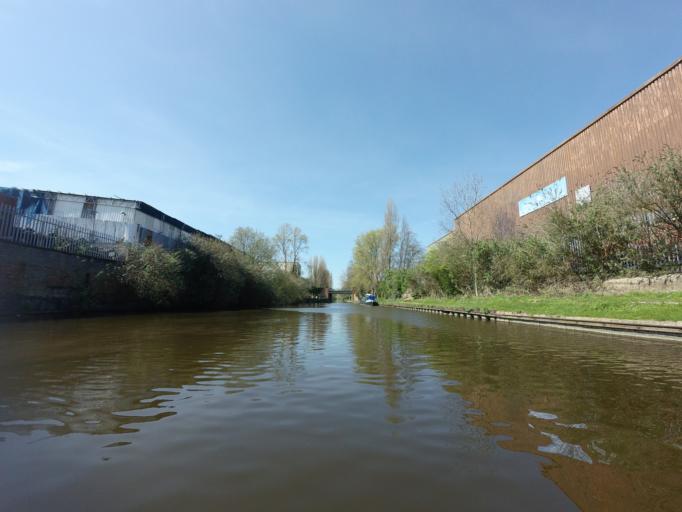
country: GB
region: England
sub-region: Greater London
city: Hayes
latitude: 51.5065
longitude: -0.4245
